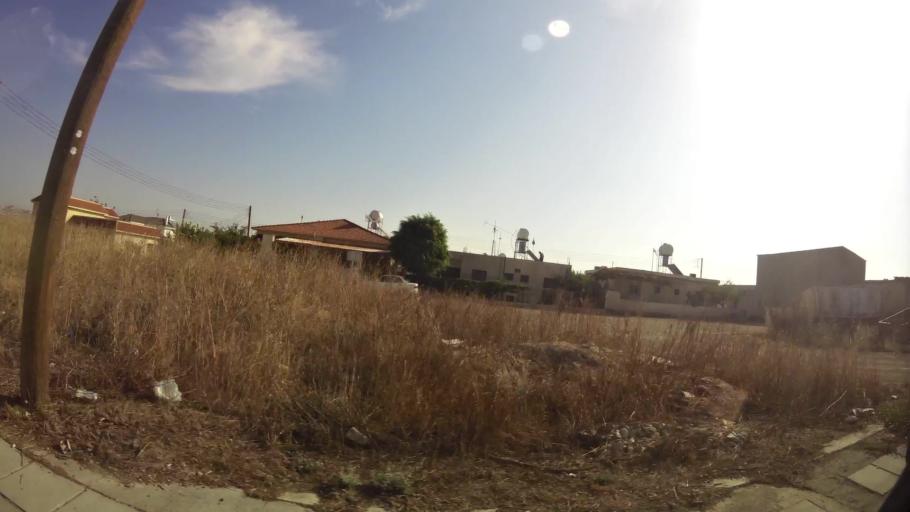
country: CY
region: Larnaka
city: Aradippou
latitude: 34.9546
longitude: 33.5961
